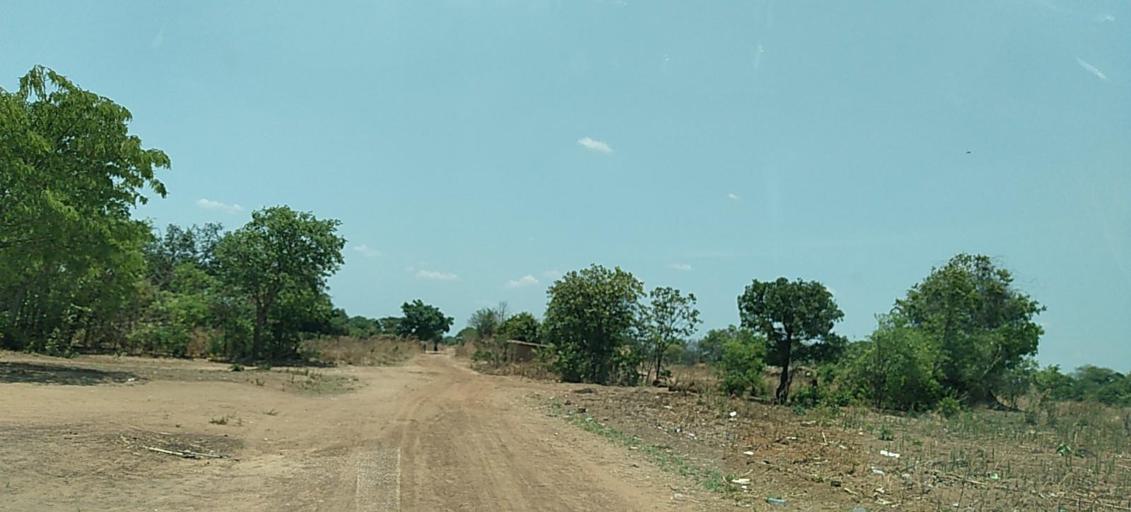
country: ZM
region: Copperbelt
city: Luanshya
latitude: -13.0890
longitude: 28.4061
